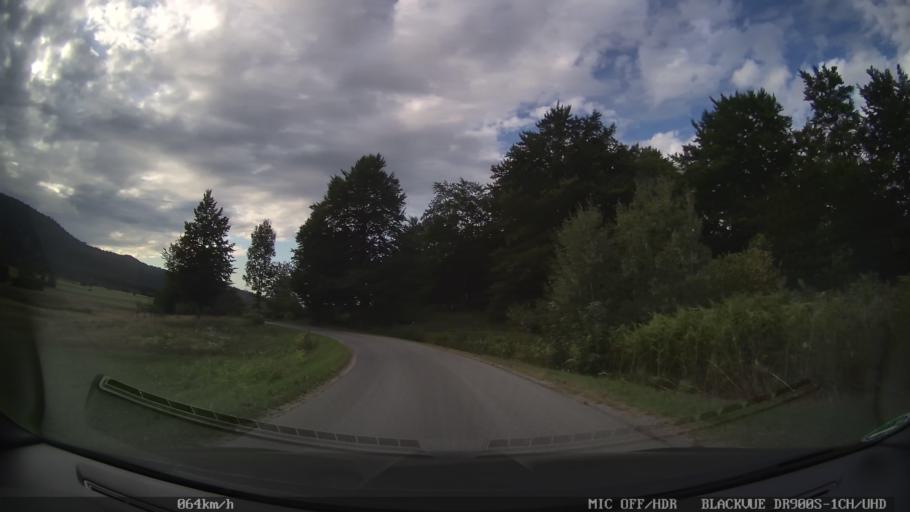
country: HR
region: Licko-Senjska
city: Jezerce
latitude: 44.9441
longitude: 15.5411
